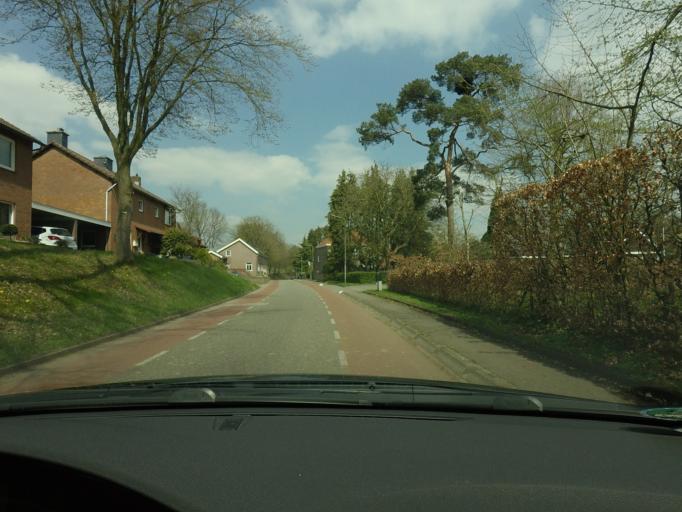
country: NL
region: Limburg
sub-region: Eijsden-Margraten
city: Margraten
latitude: 50.7815
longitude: 5.8556
